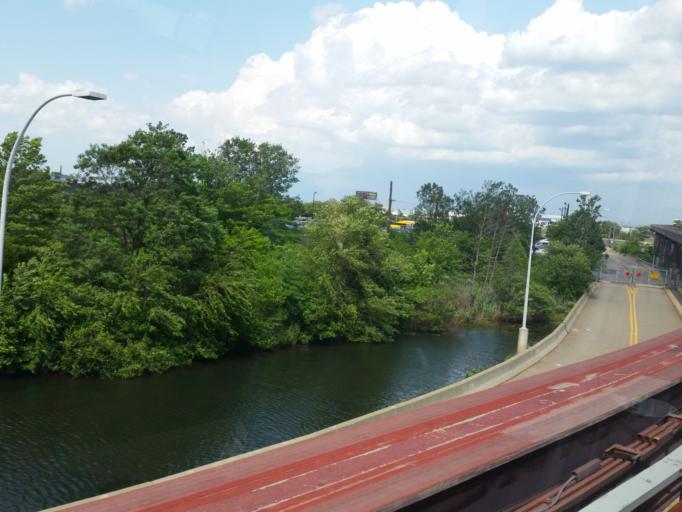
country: US
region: New Jersey
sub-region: Union County
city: Hillside
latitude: 40.6989
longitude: -74.1911
